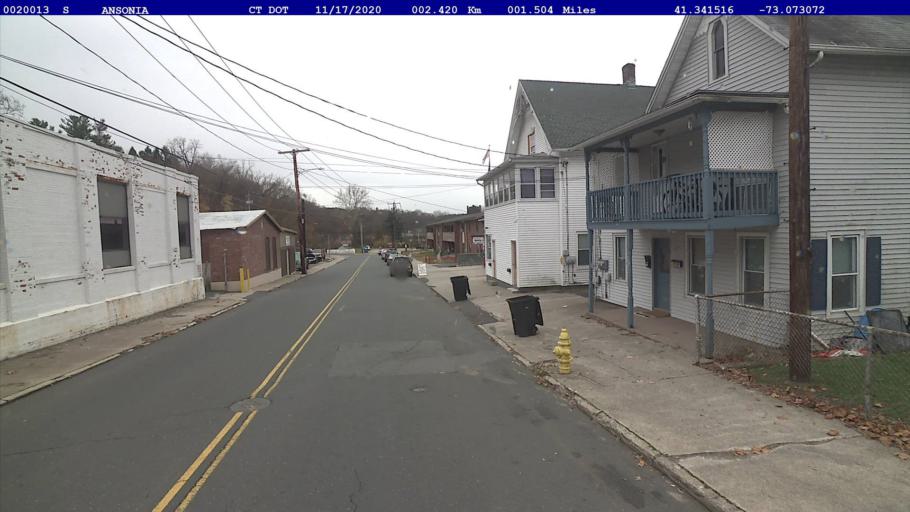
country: US
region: Connecticut
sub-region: New Haven County
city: Ansonia
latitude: 41.3415
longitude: -73.0731
